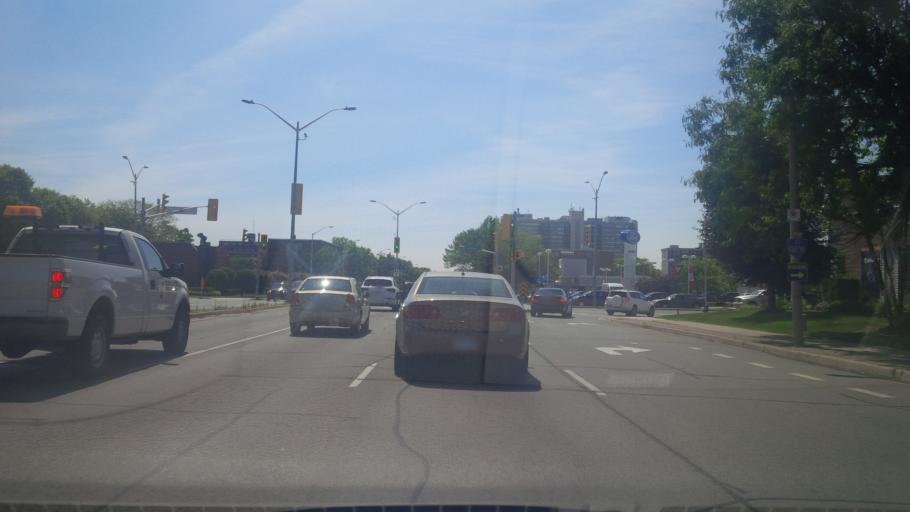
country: CA
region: Ontario
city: Burlington
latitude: 43.3363
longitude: -79.8134
